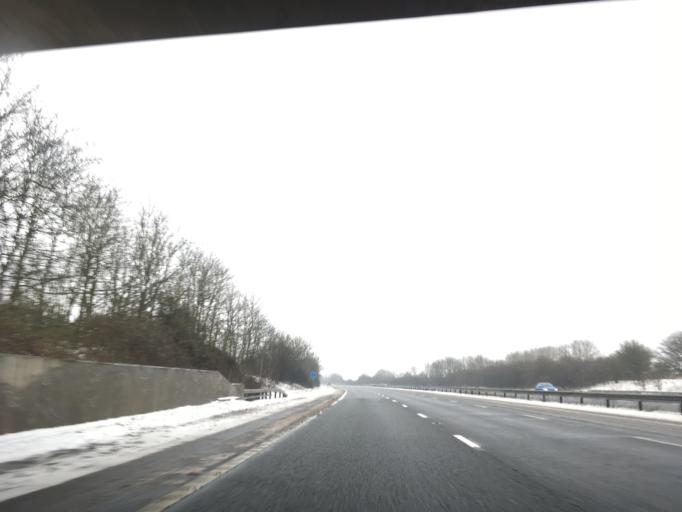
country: GB
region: England
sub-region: Gloucestershire
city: Uckington
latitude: 51.9379
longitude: -2.1299
